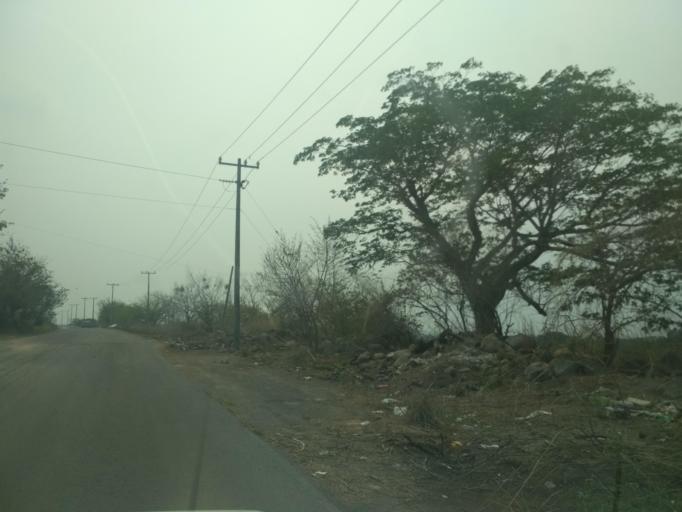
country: MX
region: Veracruz
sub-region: Veracruz
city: Delfino Victoria (Santa Fe)
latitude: 19.1869
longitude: -96.3160
